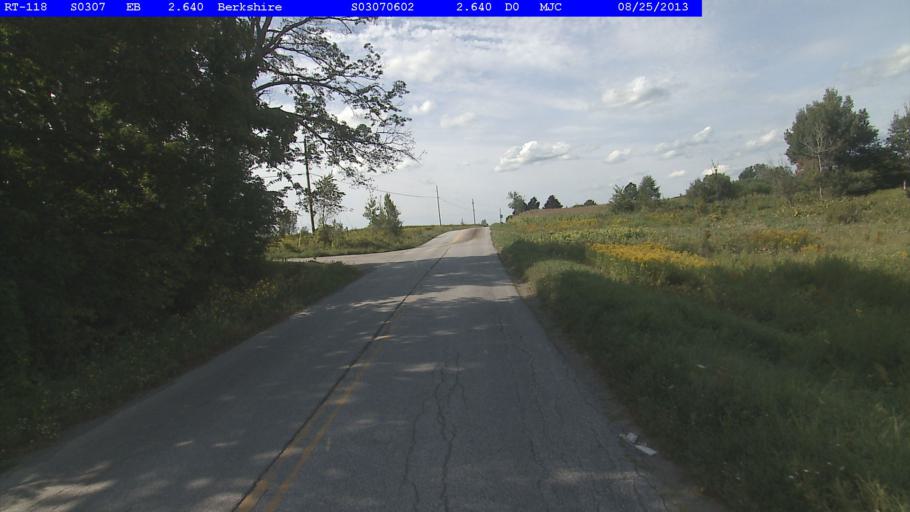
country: US
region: Vermont
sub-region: Franklin County
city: Enosburg Falls
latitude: 44.9544
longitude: -72.7529
